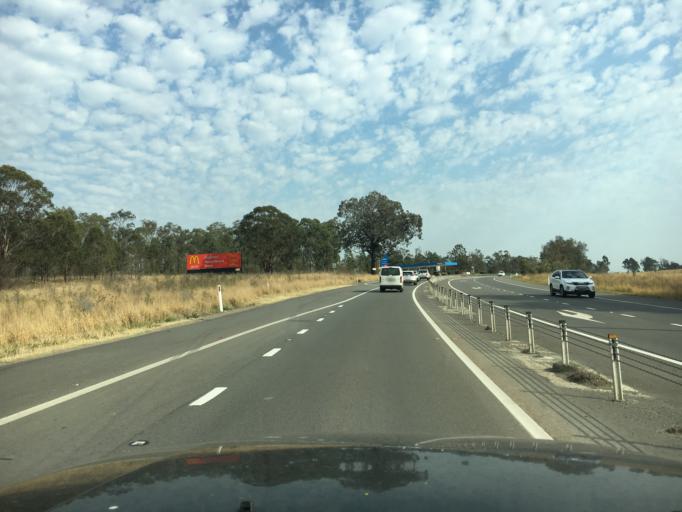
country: AU
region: New South Wales
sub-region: Singleton
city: Singleton
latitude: -32.6425
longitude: 151.2334
